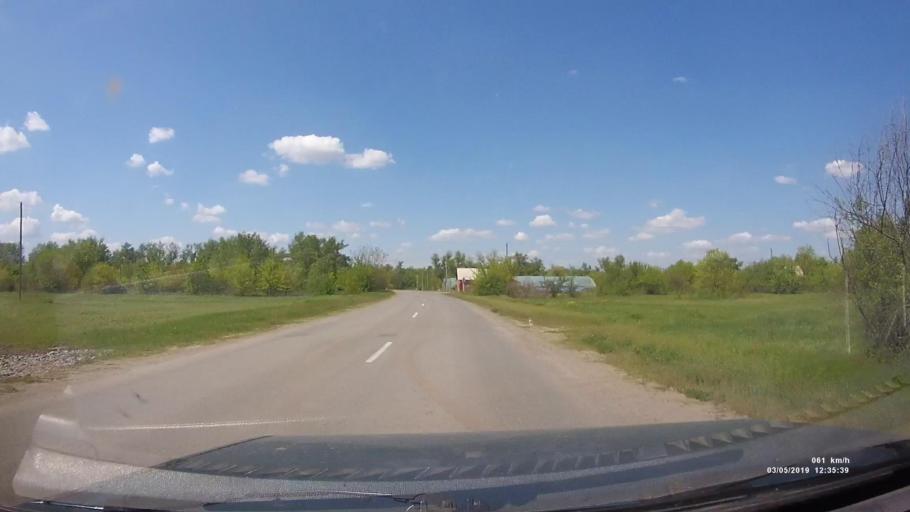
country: RU
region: Rostov
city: Semikarakorsk
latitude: 47.5282
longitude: 40.7591
